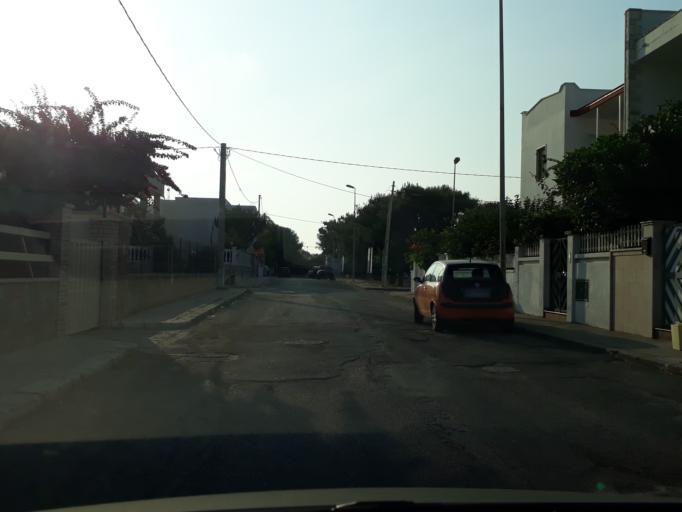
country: IT
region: Apulia
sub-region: Provincia di Brindisi
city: Carovigno
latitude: 40.7555
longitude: 17.7078
